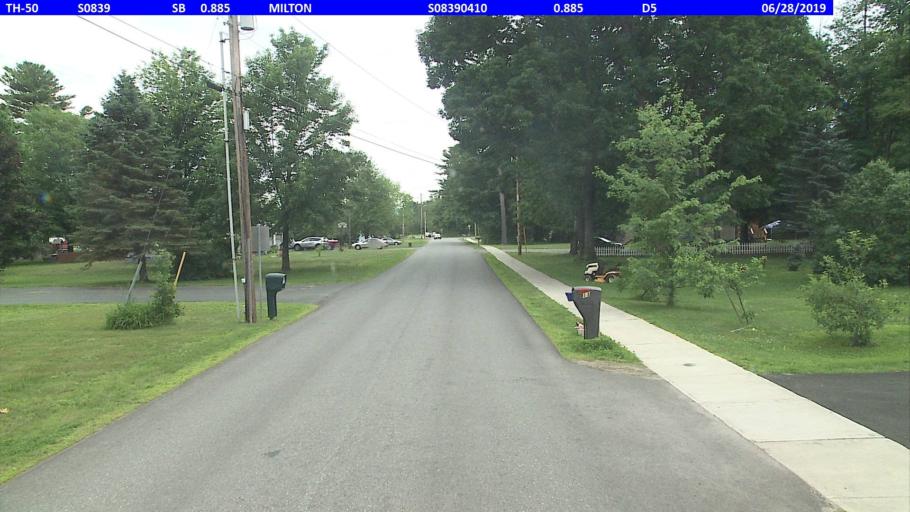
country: US
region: Vermont
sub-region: Chittenden County
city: Milton
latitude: 44.6164
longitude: -73.1114
